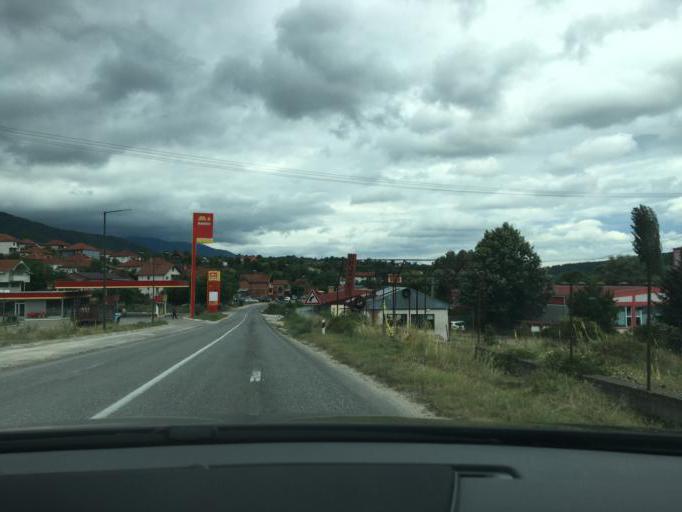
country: MK
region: Kriva Palanka
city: Kriva Palanka
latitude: 42.1899
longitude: 22.3035
